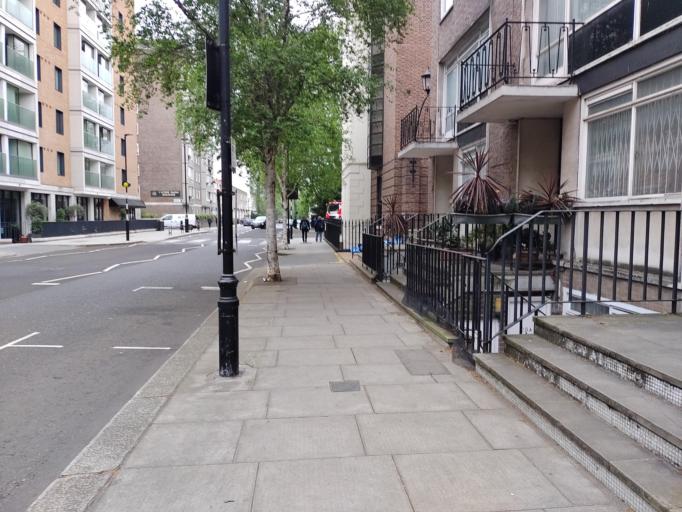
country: GB
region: England
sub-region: Greater London
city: Bayswater
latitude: 51.5147
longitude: -0.1683
